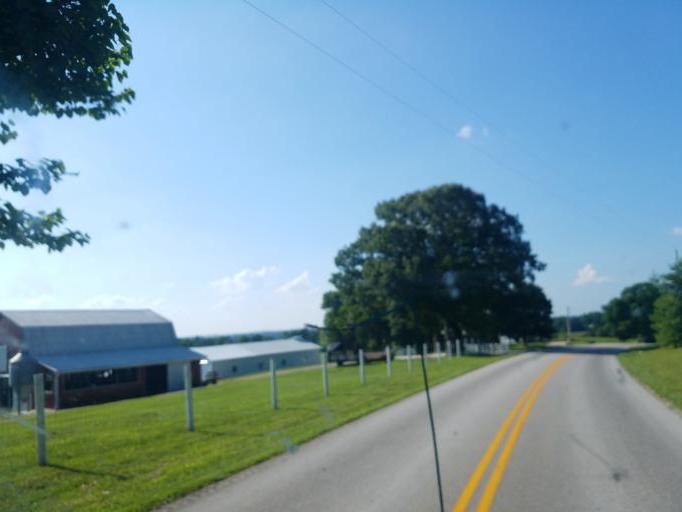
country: US
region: Kentucky
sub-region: Hart County
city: Munfordville
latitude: 37.3196
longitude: -86.0617
